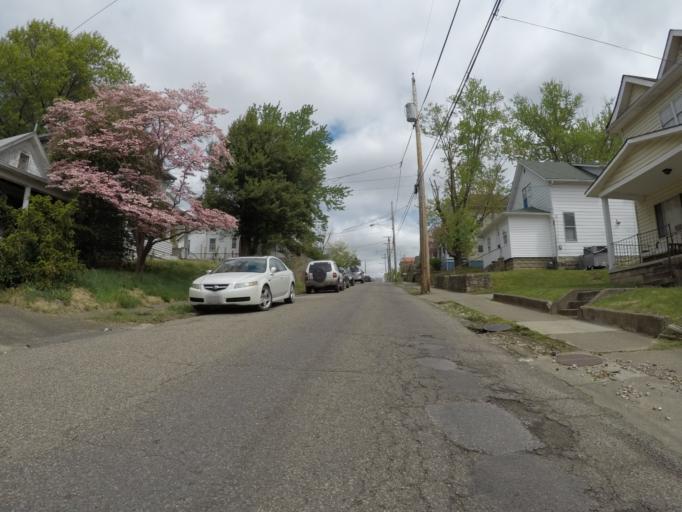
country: US
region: West Virginia
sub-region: Cabell County
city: Huntington
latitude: 38.4100
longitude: -82.4064
